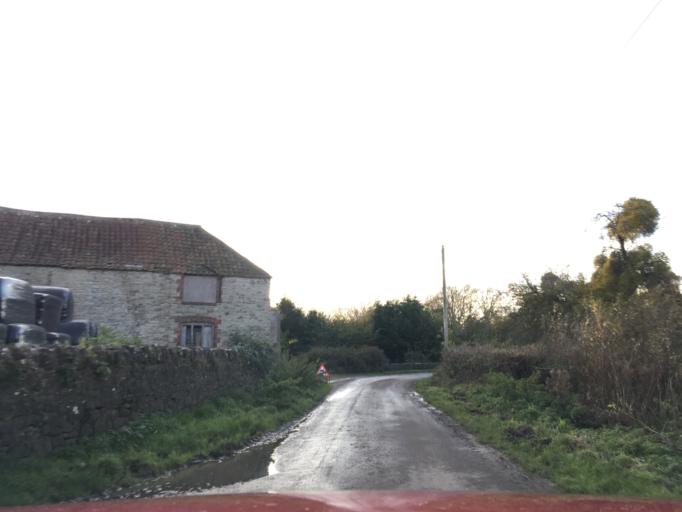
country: GB
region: England
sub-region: South Gloucestershire
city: Hill
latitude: 51.6628
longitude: -2.5524
